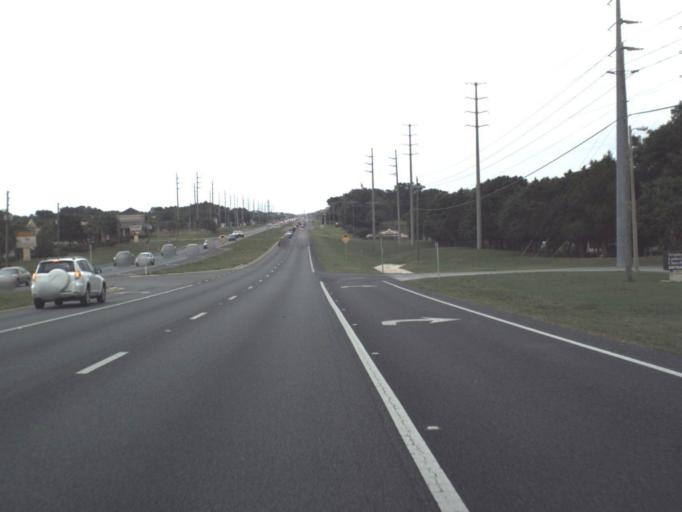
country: US
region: Florida
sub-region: Sumter County
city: The Villages
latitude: 28.9703
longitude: -81.9758
